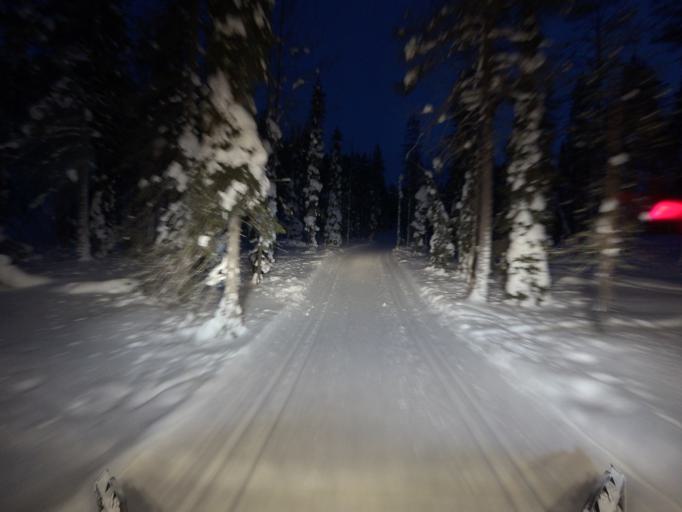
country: FI
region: Lapland
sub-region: Tunturi-Lappi
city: Kolari
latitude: 67.5976
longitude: 24.1106
